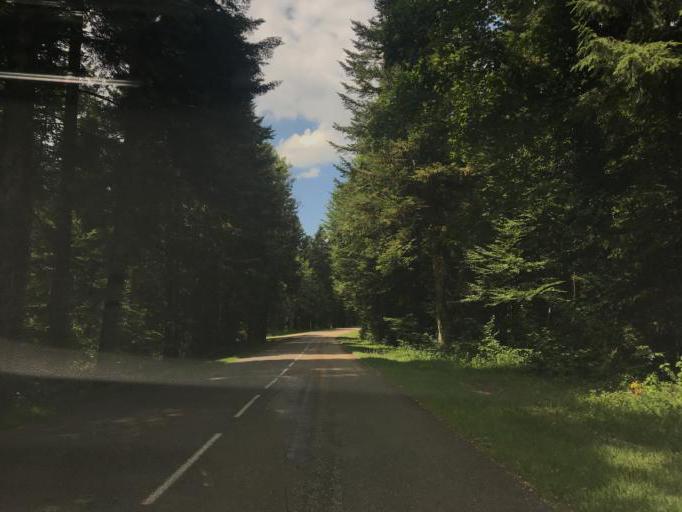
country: FR
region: Franche-Comte
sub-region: Departement du Jura
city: Clairvaux-les-Lacs
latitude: 46.5477
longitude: 5.7906
